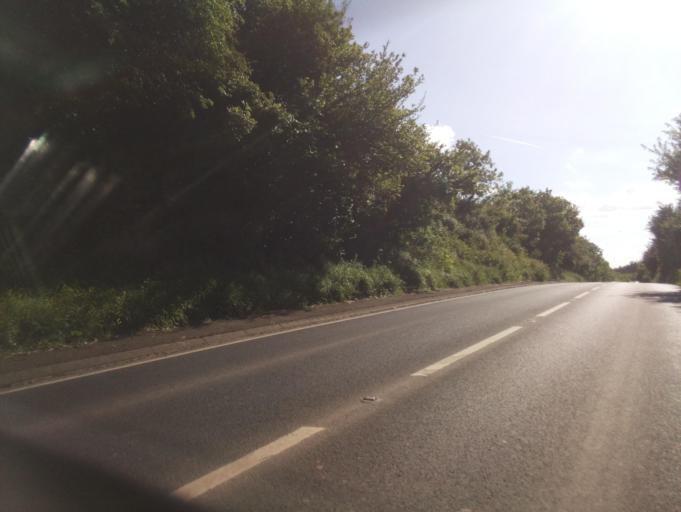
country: GB
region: England
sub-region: Somerset
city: Creech Saint Michael
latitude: 51.0480
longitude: -3.0089
